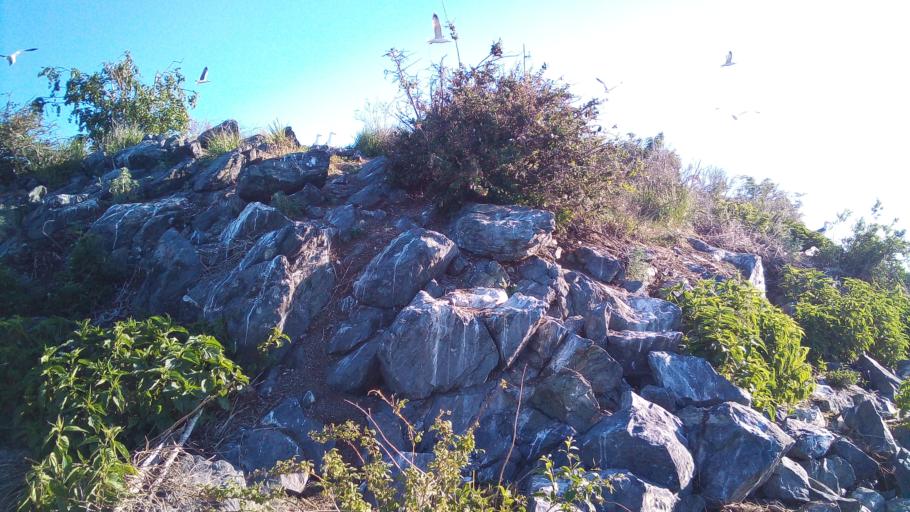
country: RU
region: Chelyabinsk
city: Karabash
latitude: 55.3578
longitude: 60.4167
